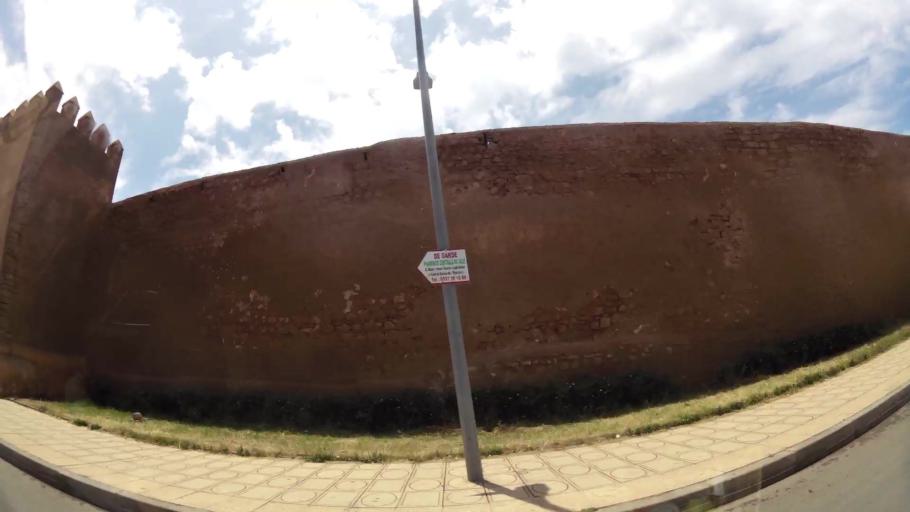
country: MA
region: Rabat-Sale-Zemmour-Zaer
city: Sale
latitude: 34.0452
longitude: -6.8265
